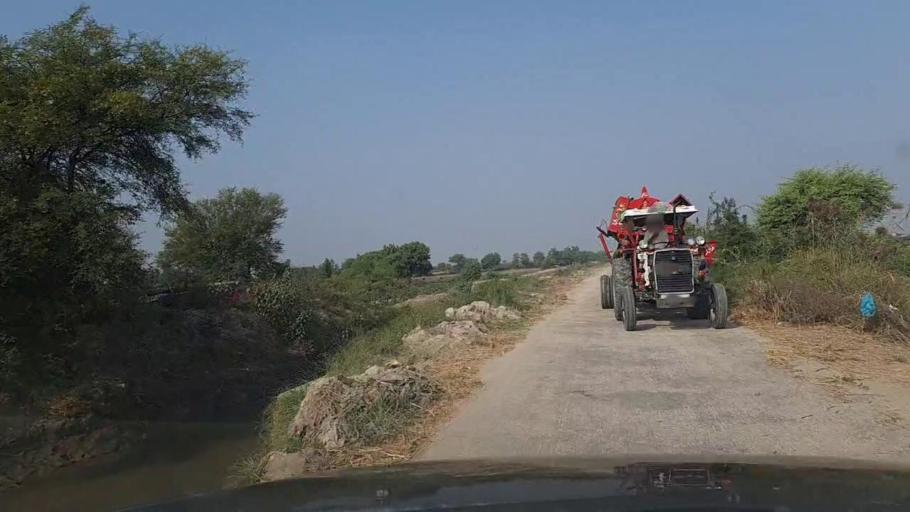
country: PK
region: Sindh
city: Mirpur Batoro
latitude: 24.7178
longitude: 68.2551
